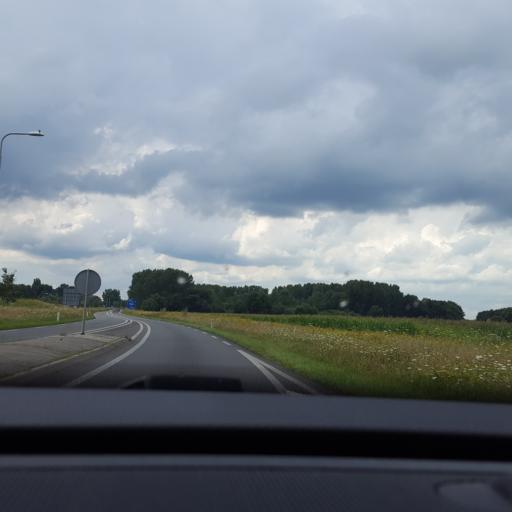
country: NL
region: Gelderland
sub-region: Gemeente Doesburg
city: Doesburg
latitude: 52.0075
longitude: 6.1575
